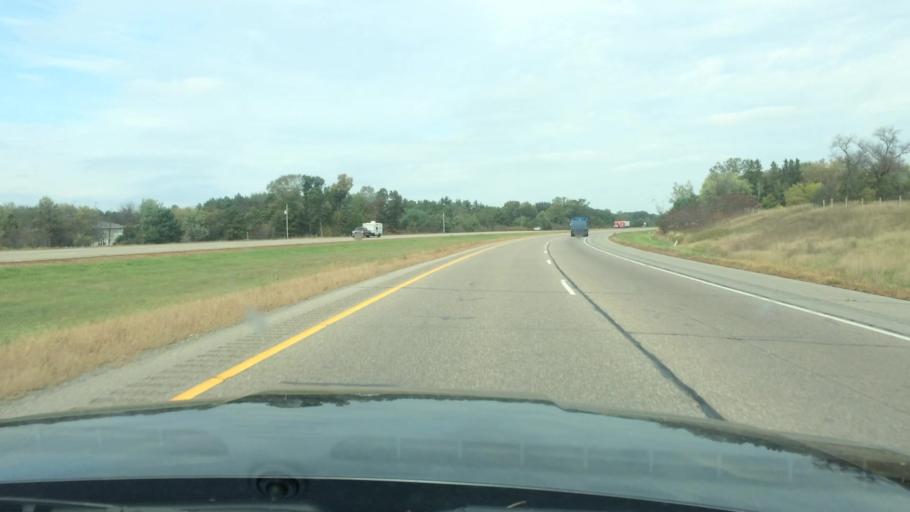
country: US
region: Wisconsin
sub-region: Marathon County
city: Mosinee
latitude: 44.6600
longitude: -89.6424
